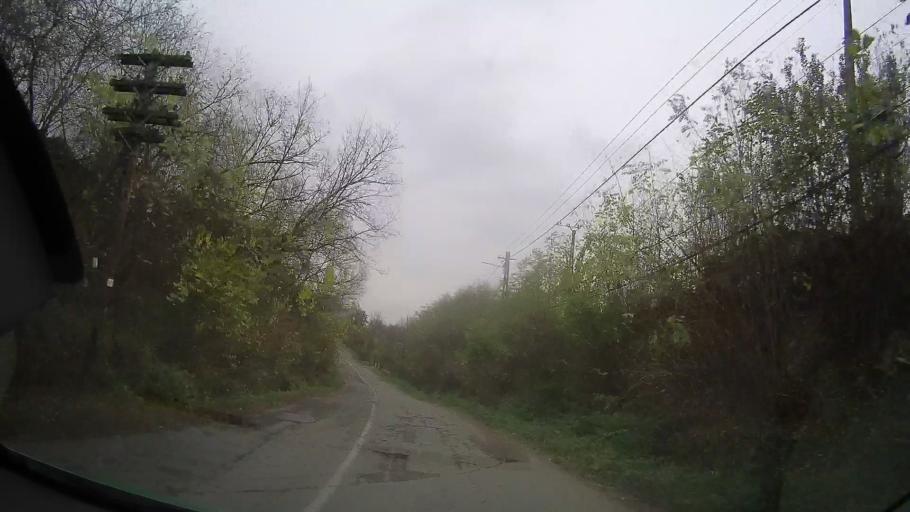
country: RO
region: Prahova
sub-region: Comuna Ceptura
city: Ceptura de Jos
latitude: 45.0330
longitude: 26.3194
